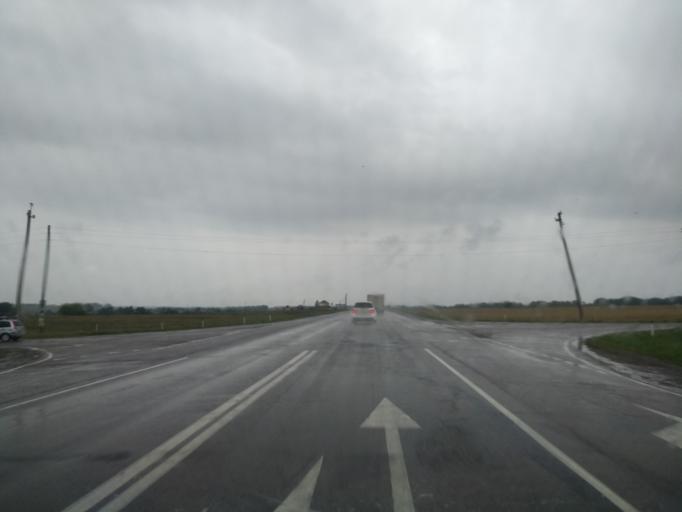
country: RU
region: Voronezj
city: Verkhnyaya Khava
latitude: 51.6781
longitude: 39.8757
